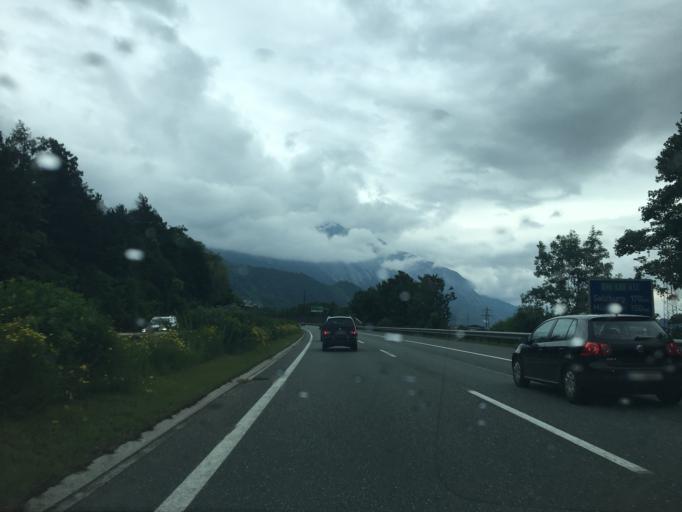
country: AT
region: Tyrol
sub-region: Politischer Bezirk Schwaz
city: Vomp
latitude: 47.3357
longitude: 11.6839
